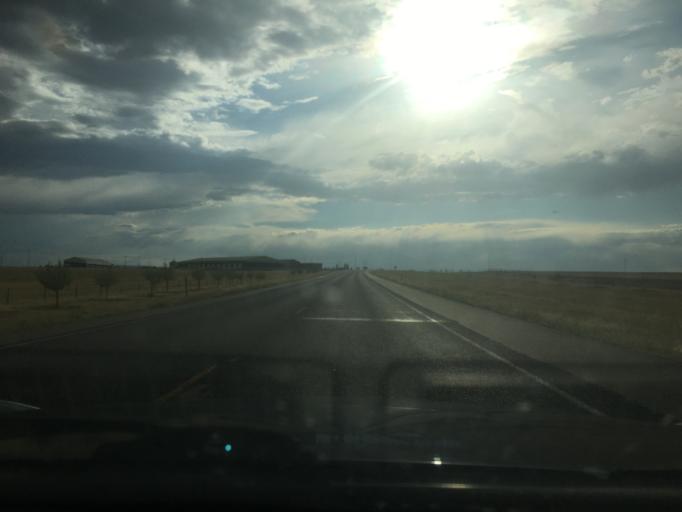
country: US
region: Wyoming
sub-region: Albany County
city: Laramie
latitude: 41.3199
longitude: -105.6487
